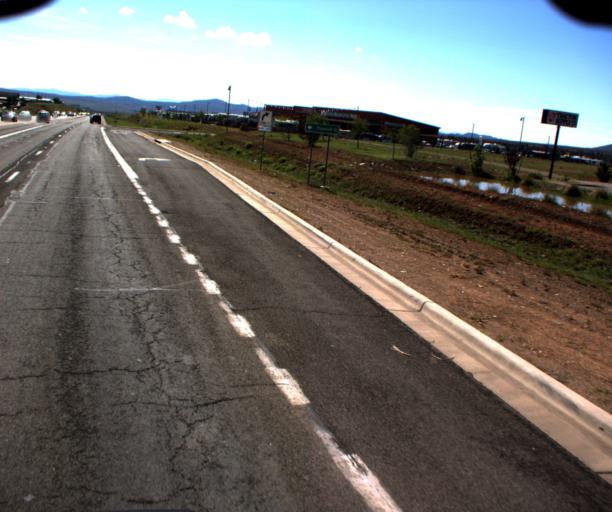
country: US
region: Arizona
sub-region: Yavapai County
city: Prescott Valley
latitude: 34.5844
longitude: -112.3131
